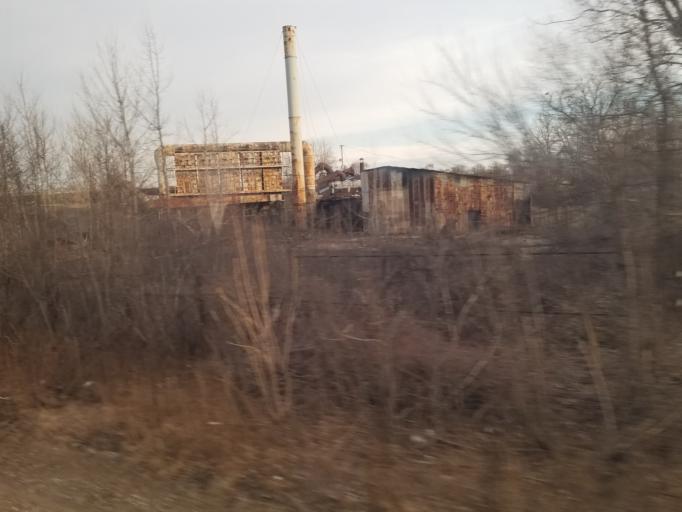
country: US
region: Indiana
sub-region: Saint Joseph County
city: South Bend
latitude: 41.6734
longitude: -86.2738
